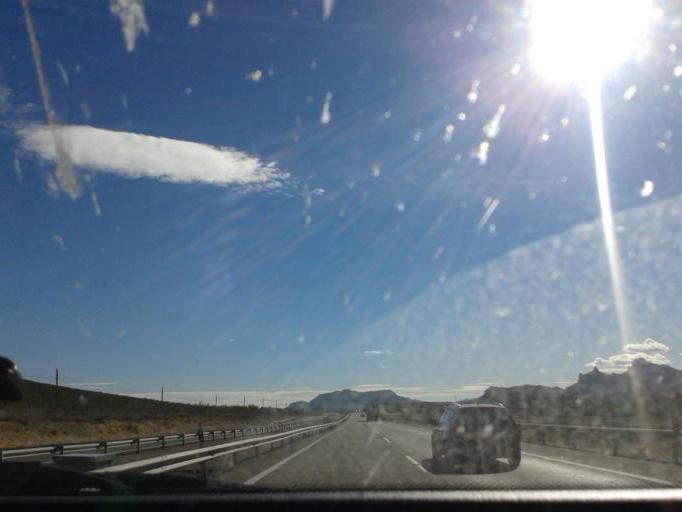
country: ES
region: Valencia
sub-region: Provincia de Alicante
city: Villena
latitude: 38.5881
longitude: -0.8437
